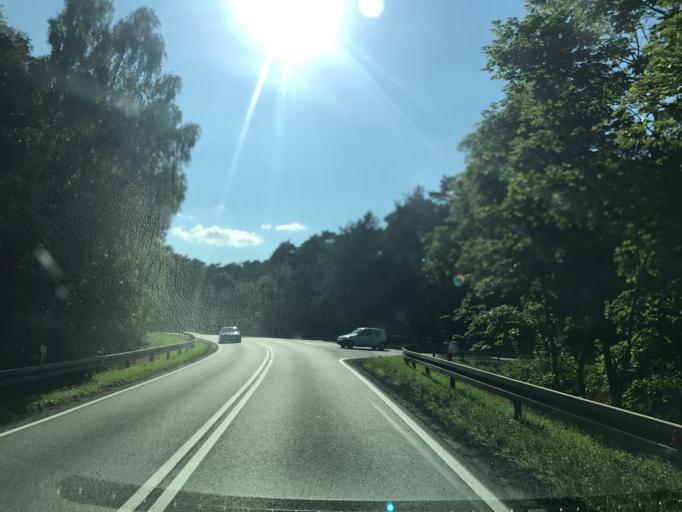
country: PL
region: Kujawsko-Pomorskie
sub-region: Wloclawek
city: Wloclawek
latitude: 52.6340
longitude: 19.0245
